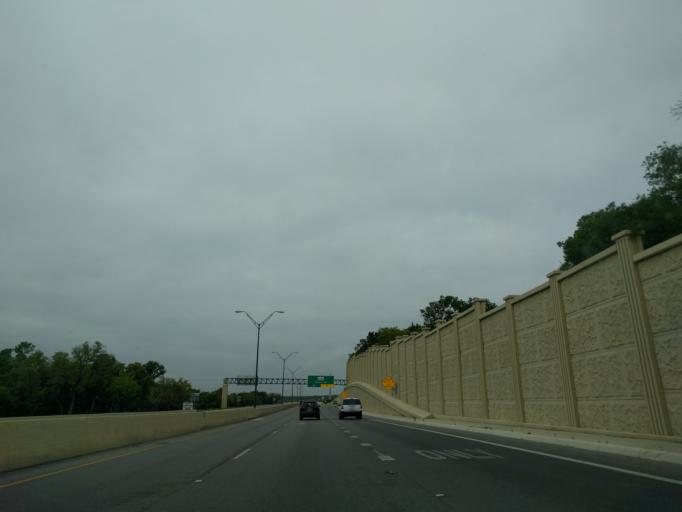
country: US
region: Texas
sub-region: Bexar County
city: Castle Hills
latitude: 29.5608
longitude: -98.5107
